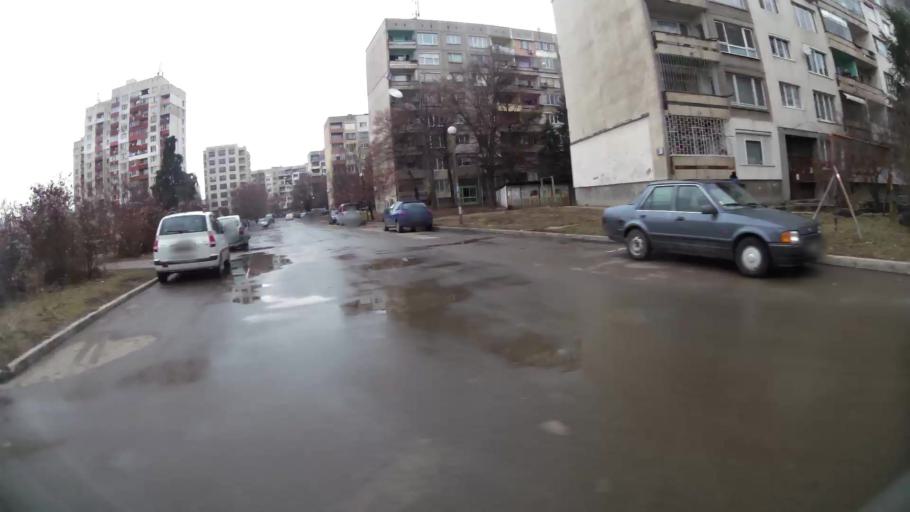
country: BG
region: Sofia-Capital
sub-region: Stolichna Obshtina
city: Sofia
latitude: 42.7249
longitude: 23.2951
